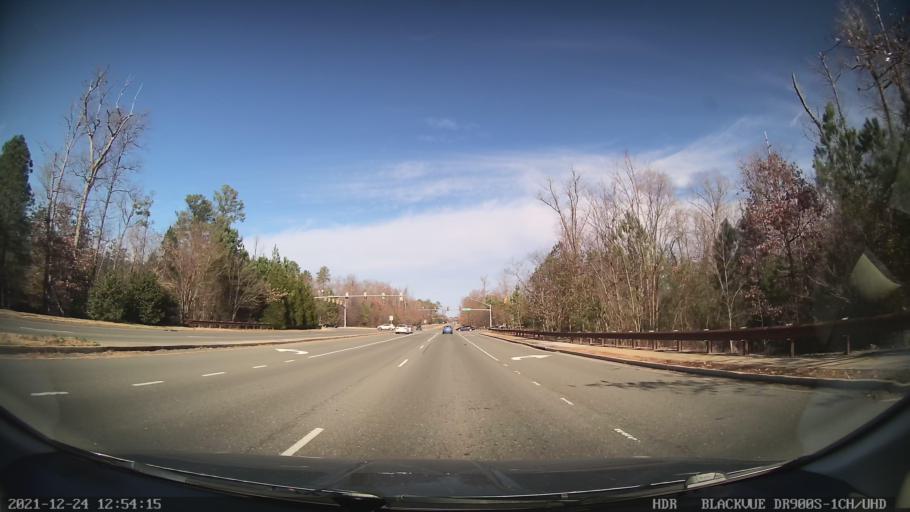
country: US
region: Virginia
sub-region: Henrico County
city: Short Pump
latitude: 37.6439
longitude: -77.6106
